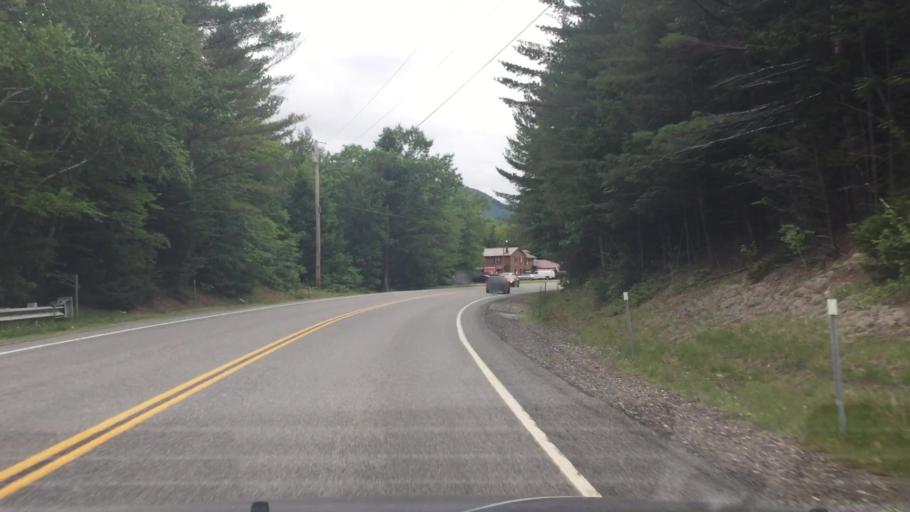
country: US
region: New Hampshire
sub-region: Carroll County
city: North Conway
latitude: 44.1358
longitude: -71.3604
